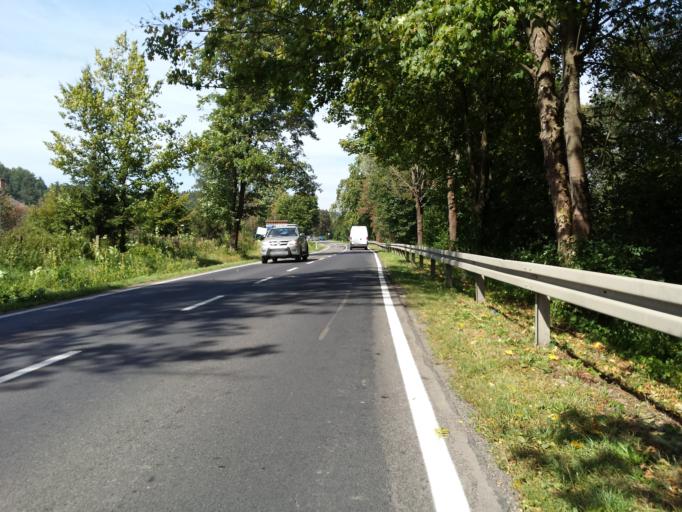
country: PL
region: Subcarpathian Voivodeship
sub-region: Powiat leski
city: Lesko
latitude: 49.4609
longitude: 22.3328
